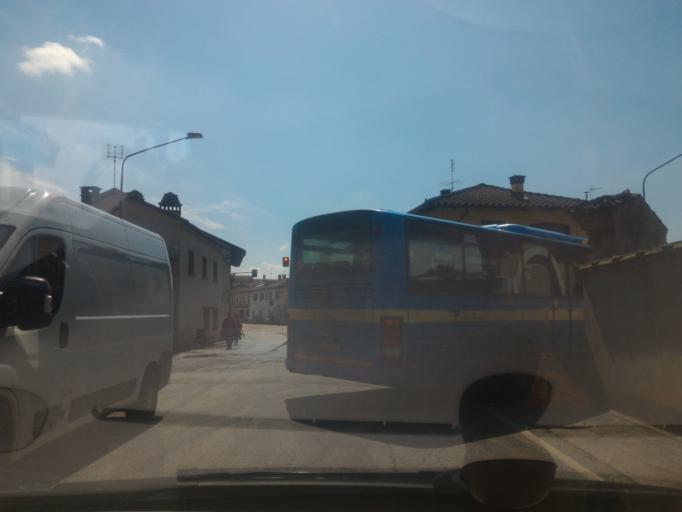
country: IT
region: Piedmont
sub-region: Provincia di Torino
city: Pancalieri
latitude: 44.8333
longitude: 7.5906
